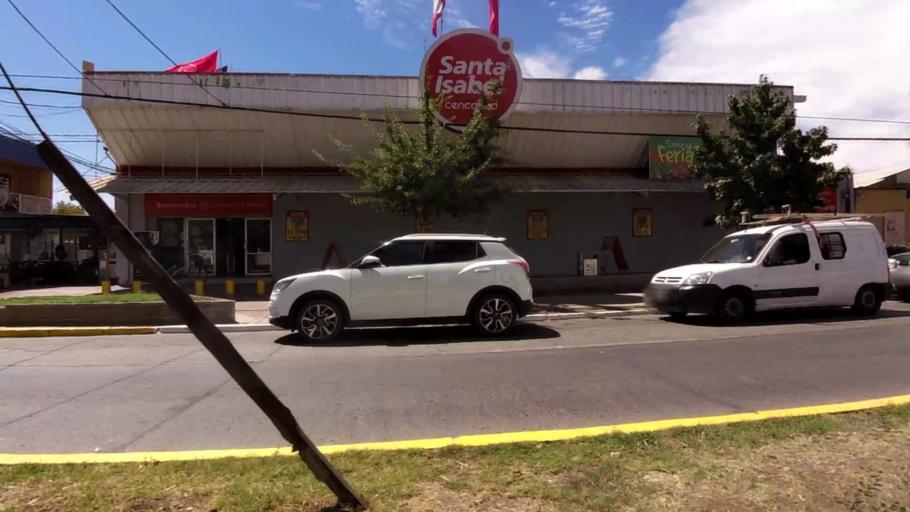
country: CL
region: O'Higgins
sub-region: Provincia de Cachapoal
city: Graneros
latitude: -33.9833
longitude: -70.7136
